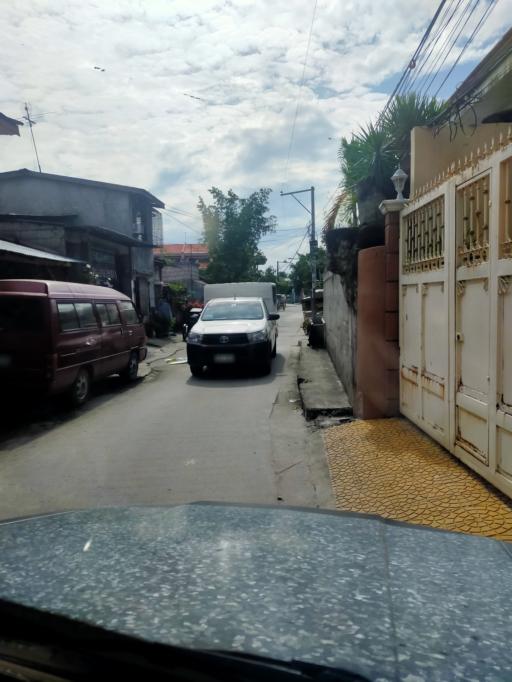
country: PH
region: Central Luzon
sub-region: Province of Pampanga
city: Pau
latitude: 15.0121
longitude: 120.7124
